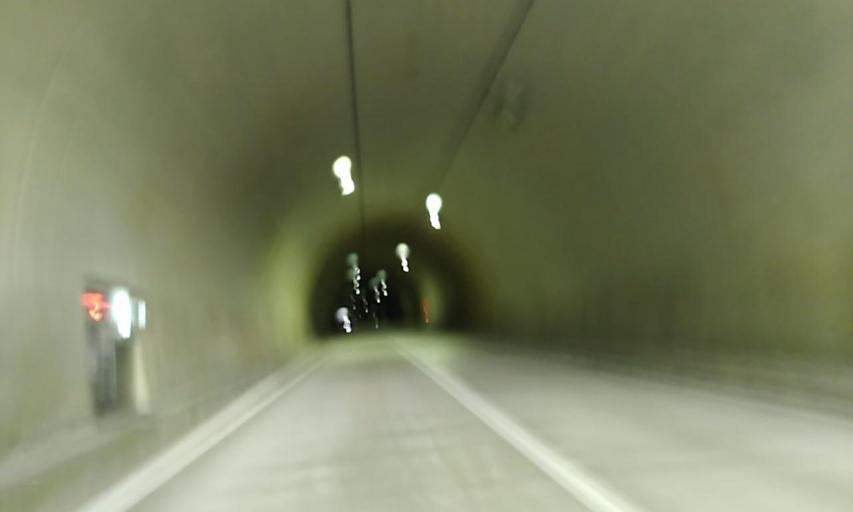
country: JP
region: Wakayama
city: Shingu
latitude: 33.8807
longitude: 135.8773
